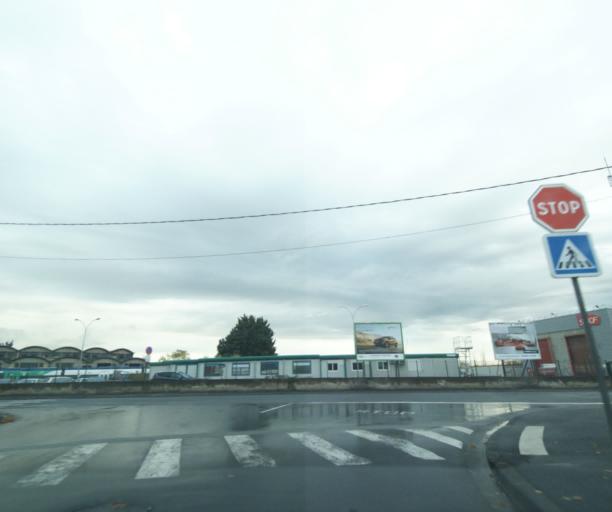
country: FR
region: Auvergne
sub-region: Departement du Puy-de-Dome
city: Aulnat
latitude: 45.7902
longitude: 3.1348
